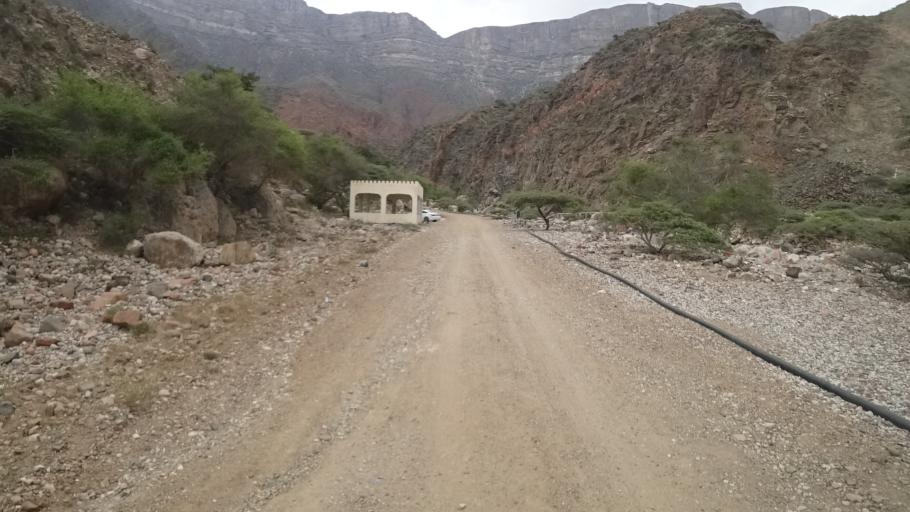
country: OM
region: Zufar
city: Salalah
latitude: 17.1845
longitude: 54.9443
